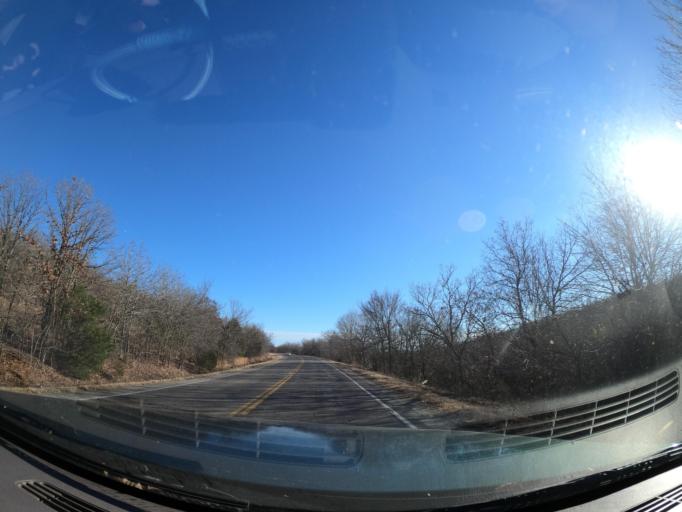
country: US
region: Oklahoma
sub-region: Pittsburg County
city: Longtown
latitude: 35.2203
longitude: -95.4281
